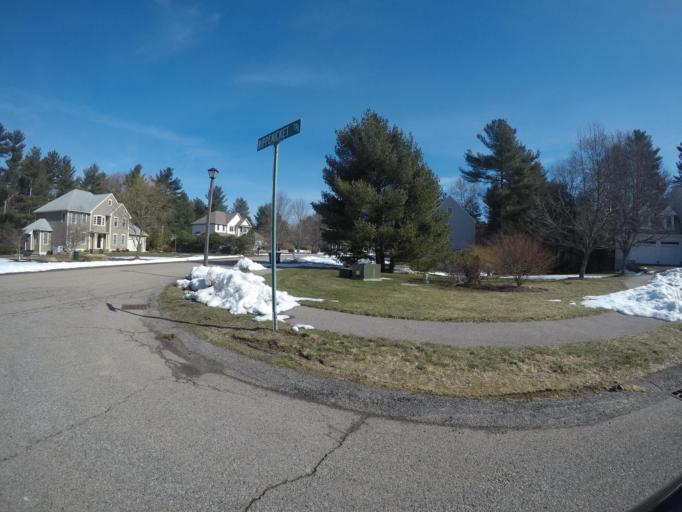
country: US
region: Massachusetts
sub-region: Bristol County
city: Easton
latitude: 41.9993
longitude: -71.1153
